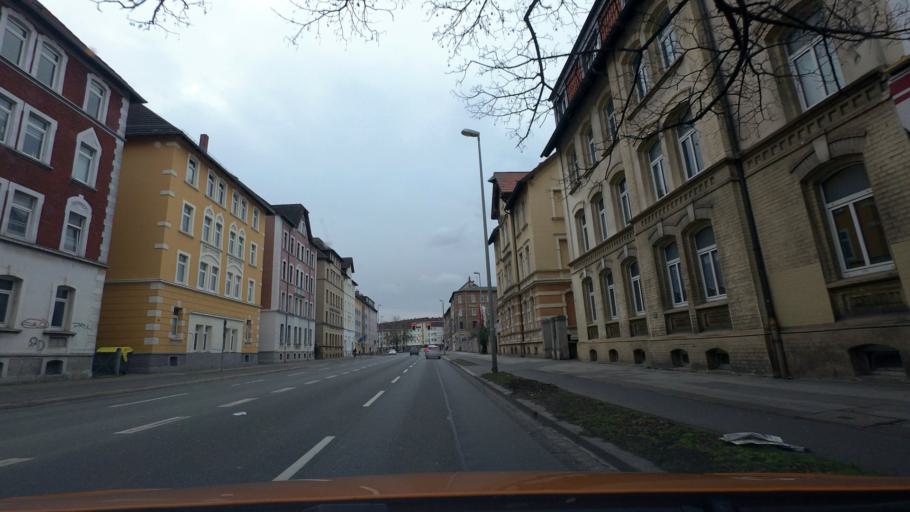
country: DE
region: Lower Saxony
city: Braunschweig
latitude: 52.2716
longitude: 10.5032
